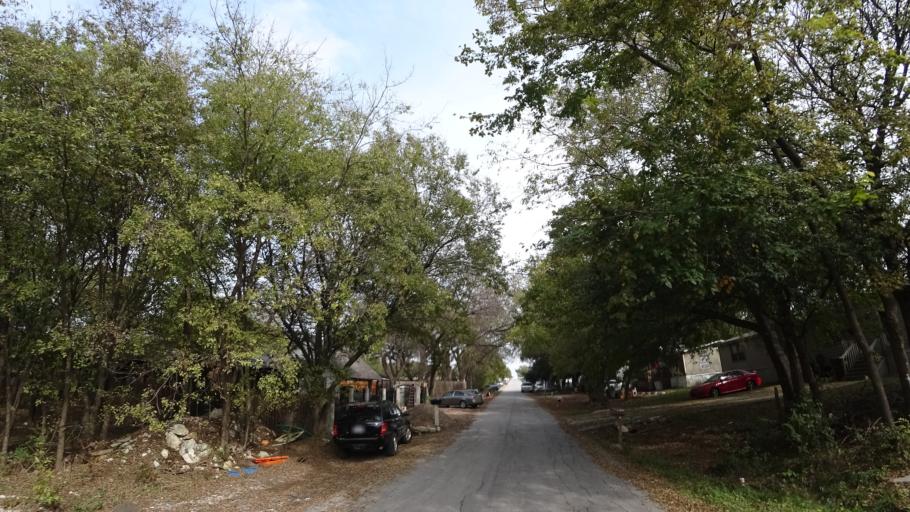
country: US
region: Texas
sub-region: Travis County
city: Wells Branch
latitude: 30.4501
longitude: -97.6728
